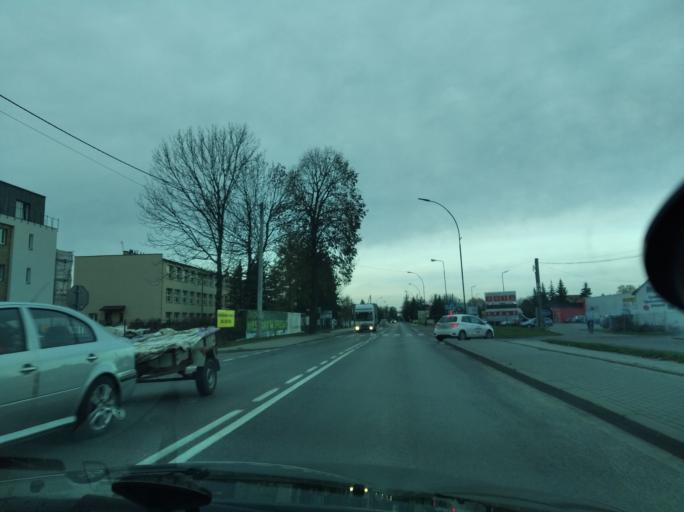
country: PL
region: Subcarpathian Voivodeship
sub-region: Powiat lancucki
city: Lancut
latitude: 50.0905
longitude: 22.2318
